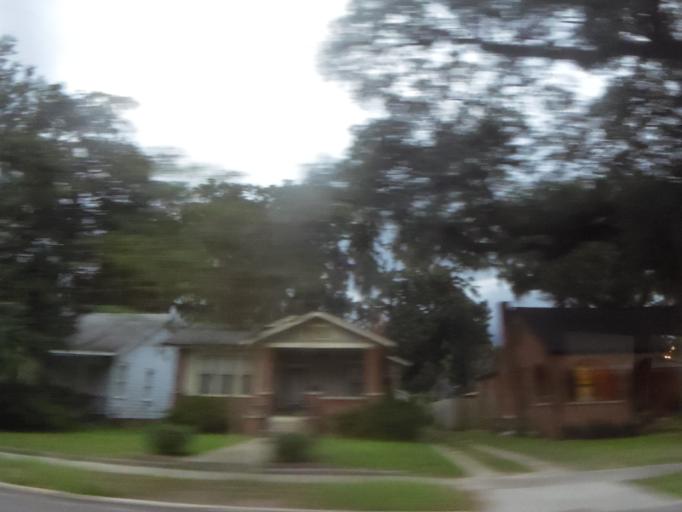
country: US
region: Florida
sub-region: Duval County
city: Jacksonville
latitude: 30.2991
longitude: -81.7057
